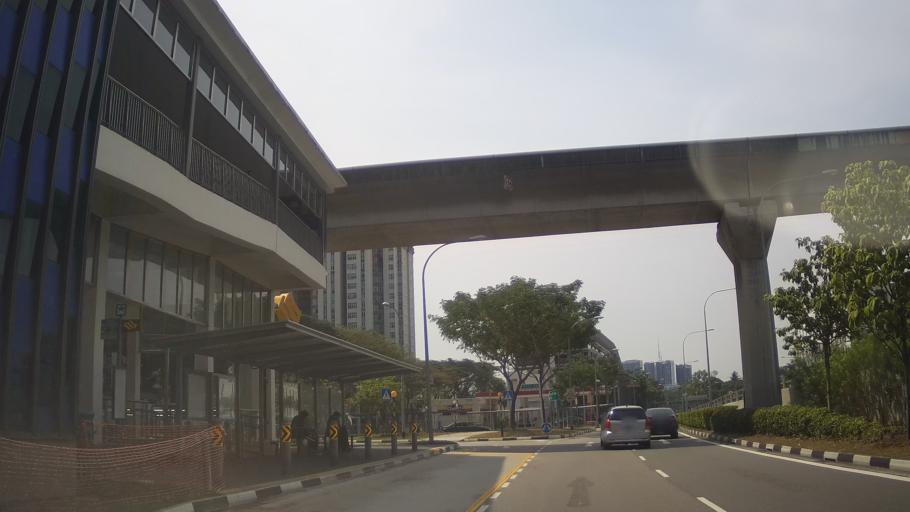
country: MY
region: Johor
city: Johor Bahru
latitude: 1.3781
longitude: 103.7622
